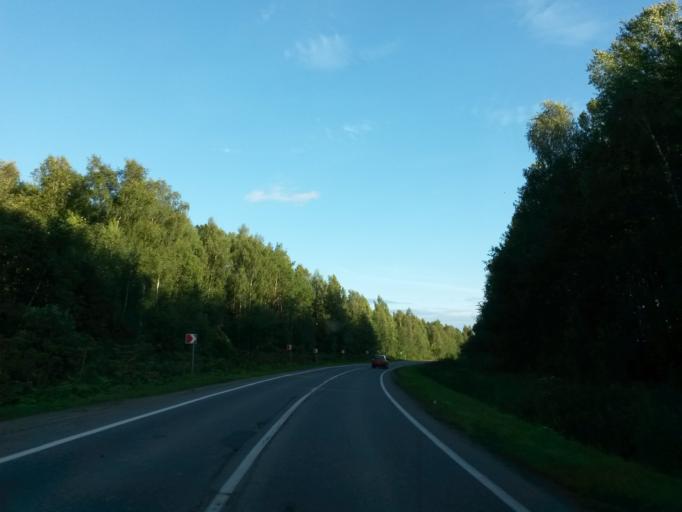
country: RU
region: Jaroslavl
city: Yaroslavl
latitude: 57.8008
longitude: 39.8268
